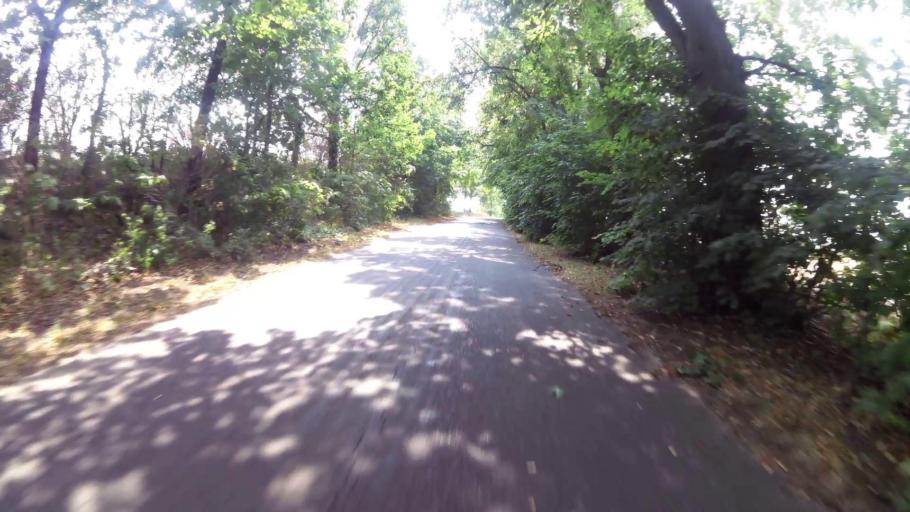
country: PL
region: West Pomeranian Voivodeship
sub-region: Powiat gryfinski
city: Mieszkowice
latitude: 52.8830
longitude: 14.5281
